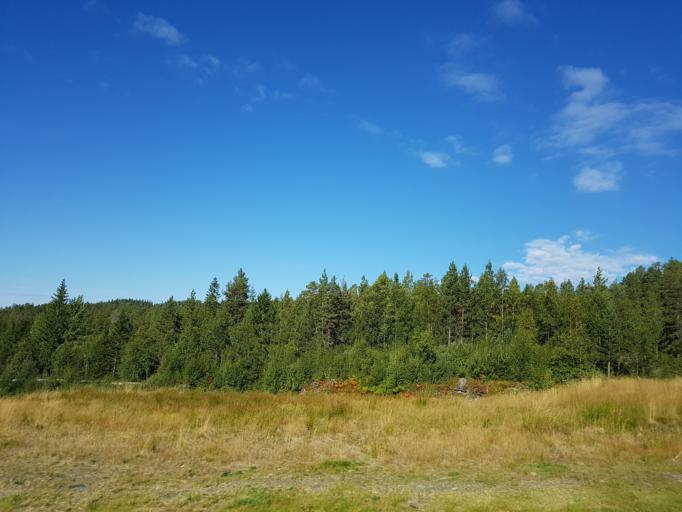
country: NO
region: Sor-Trondelag
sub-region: Trondheim
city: Trondheim
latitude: 63.6352
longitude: 10.2682
